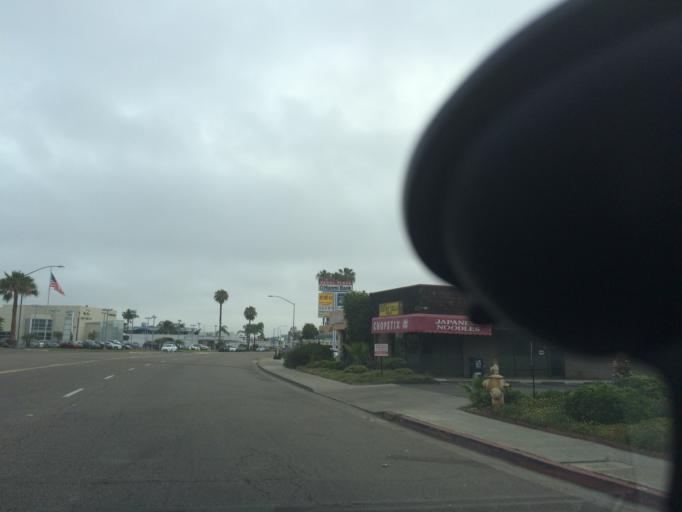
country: US
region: California
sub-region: San Diego County
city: San Diego
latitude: 32.8245
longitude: -117.1551
